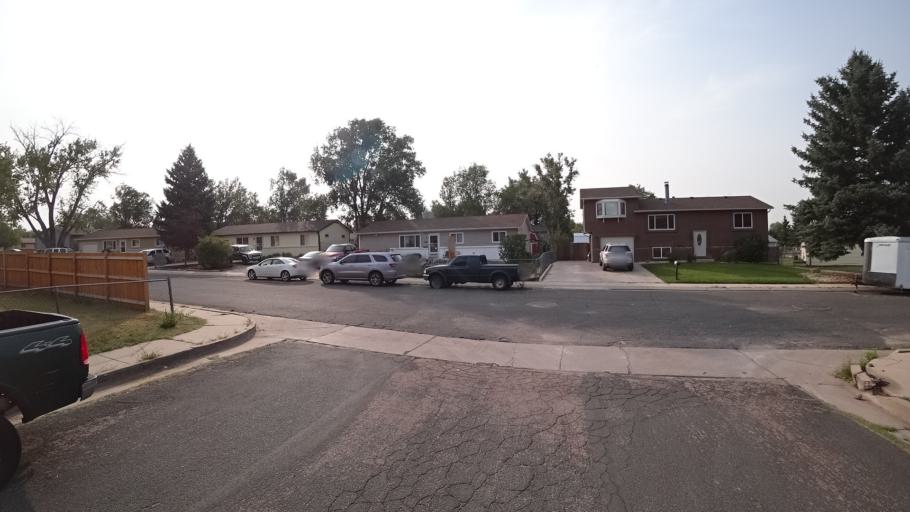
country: US
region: Colorado
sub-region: El Paso County
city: Stratmoor
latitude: 38.7997
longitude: -104.7475
